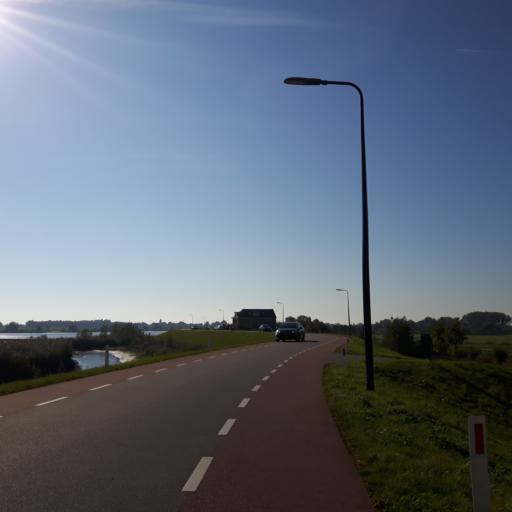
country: NL
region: South Holland
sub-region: Molenwaard
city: Liesveld
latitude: 51.9408
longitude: 4.8275
